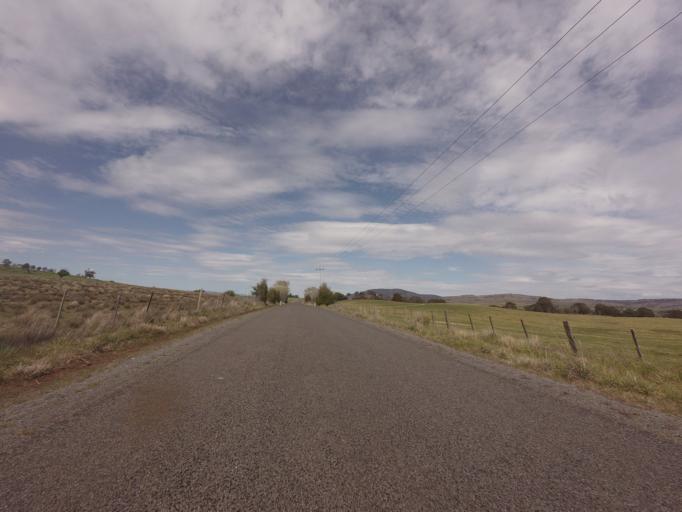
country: AU
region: Tasmania
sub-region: Northern Midlands
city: Evandale
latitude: -41.8825
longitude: 147.3643
